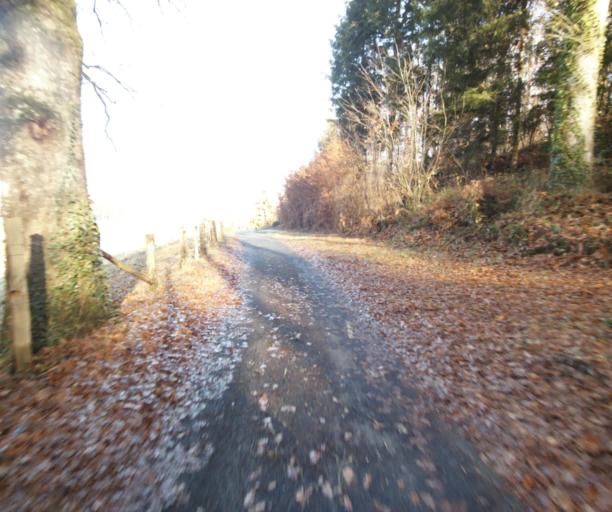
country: FR
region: Limousin
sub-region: Departement de la Correze
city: Laguenne
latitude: 45.2436
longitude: 1.7651
